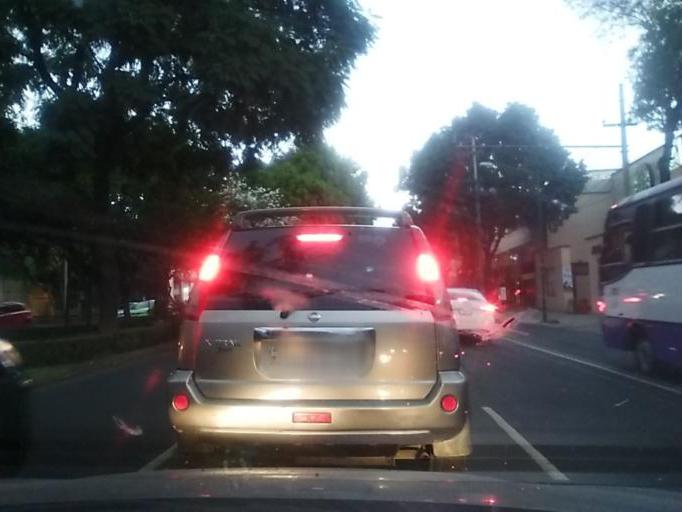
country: MX
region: Mexico City
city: Coyoacan
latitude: 19.3461
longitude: -99.1761
